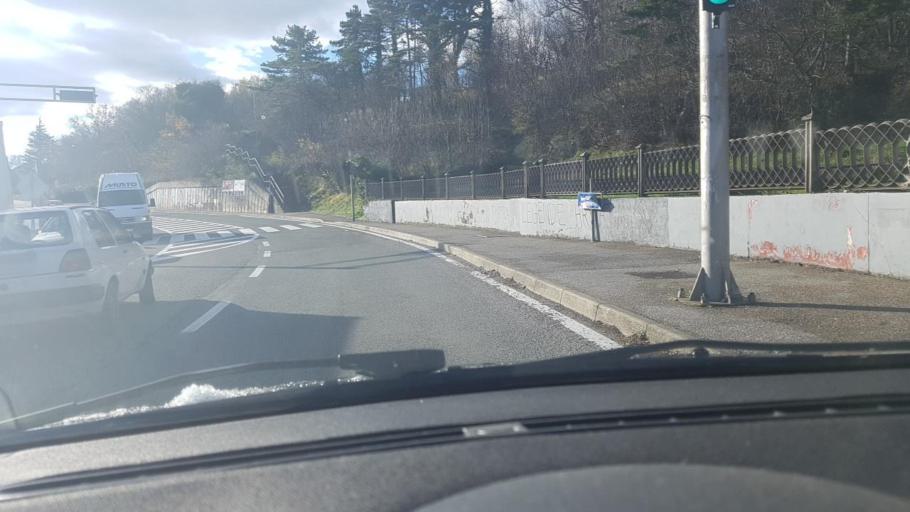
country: HR
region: Primorsko-Goranska
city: Cavle
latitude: 45.3551
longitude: 14.4856
